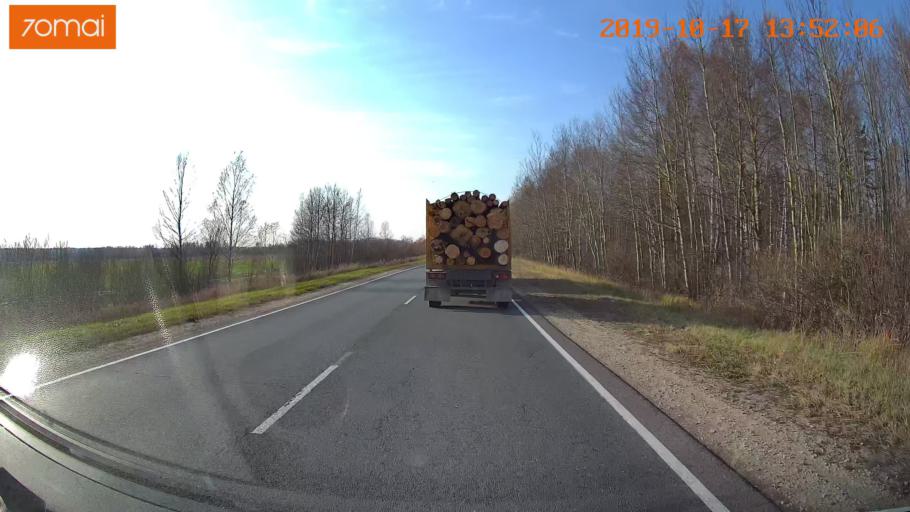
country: RU
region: Rjazan
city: Tuma
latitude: 55.1400
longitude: 40.3738
